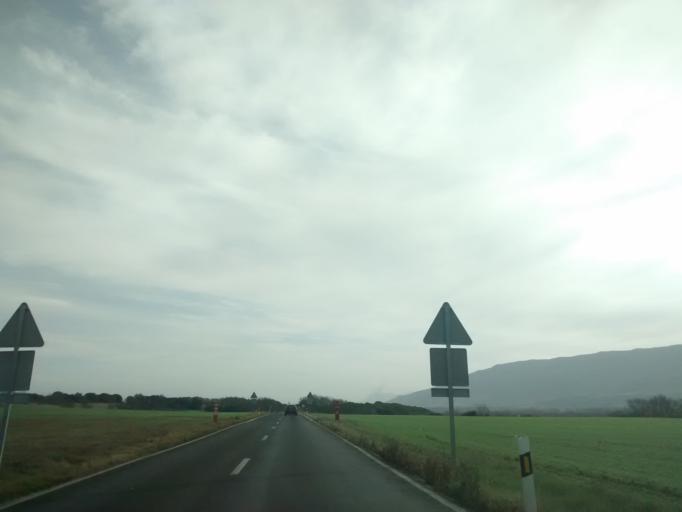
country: ES
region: Aragon
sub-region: Provincia de Zaragoza
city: Siguees
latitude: 42.6118
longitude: -1.0522
